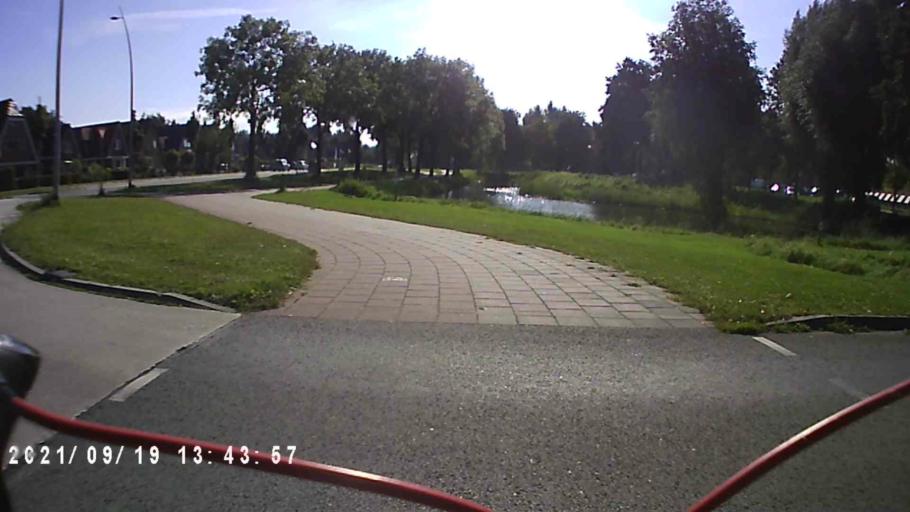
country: NL
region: Groningen
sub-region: Gemeente  Oldambt
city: Winschoten
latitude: 53.1342
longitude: 7.0431
